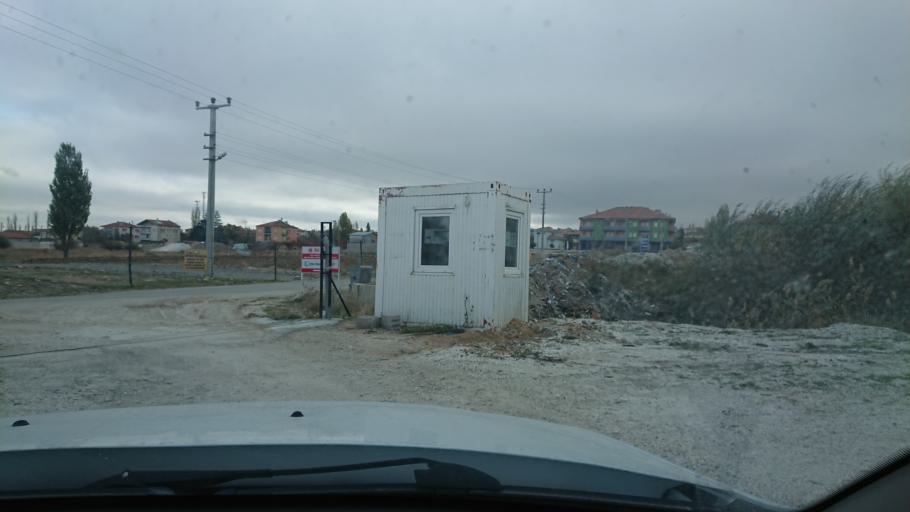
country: TR
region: Aksaray
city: Ortakoy
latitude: 38.7447
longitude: 34.0486
